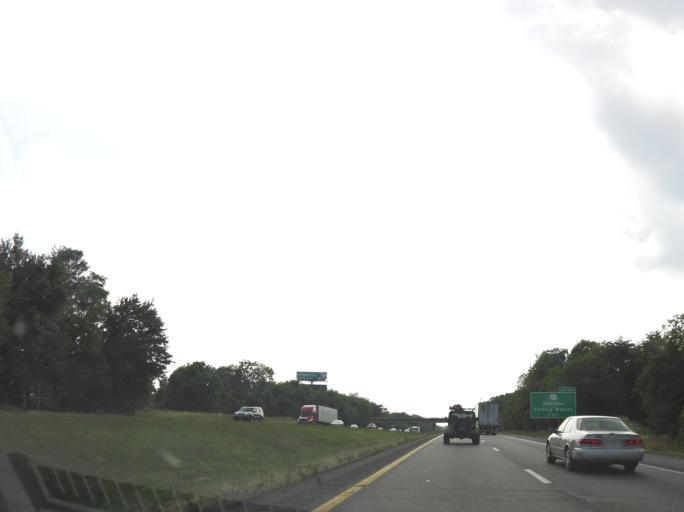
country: US
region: Maryland
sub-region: Washington County
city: Williamsport
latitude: 39.5847
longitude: -77.8529
